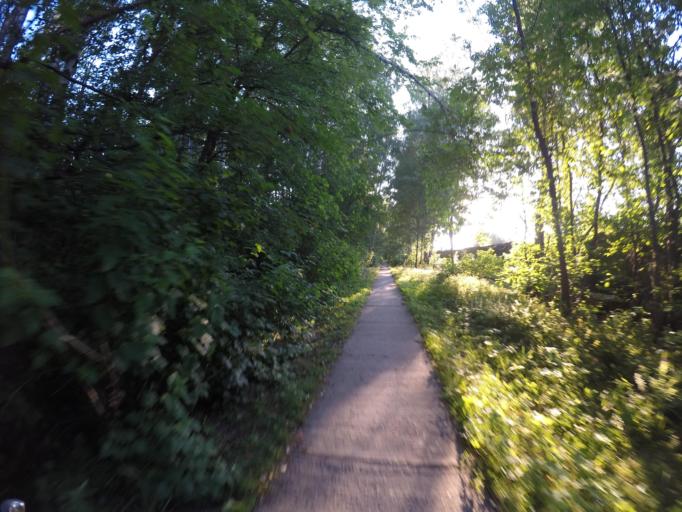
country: RU
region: Moskovskaya
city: Rechitsy
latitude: 55.6045
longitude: 38.5005
